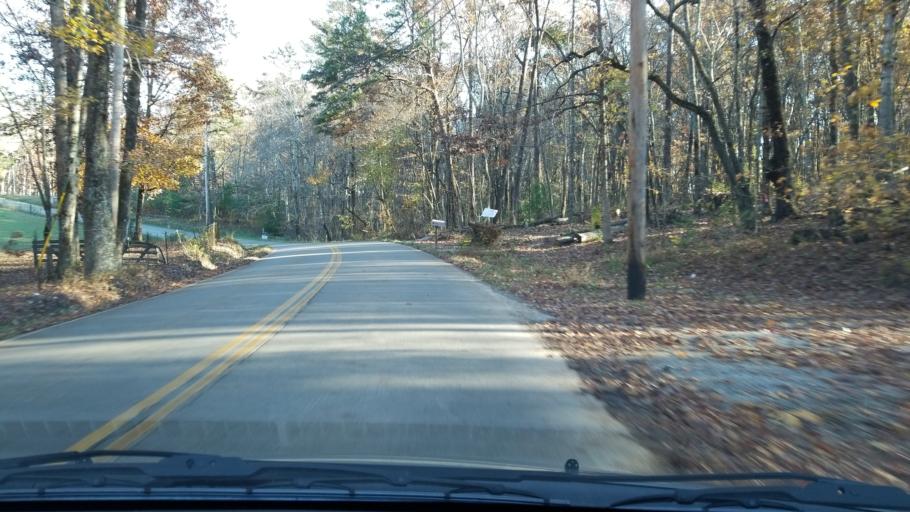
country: US
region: Tennessee
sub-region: Hamilton County
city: Falling Water
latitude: 35.2190
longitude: -85.2760
